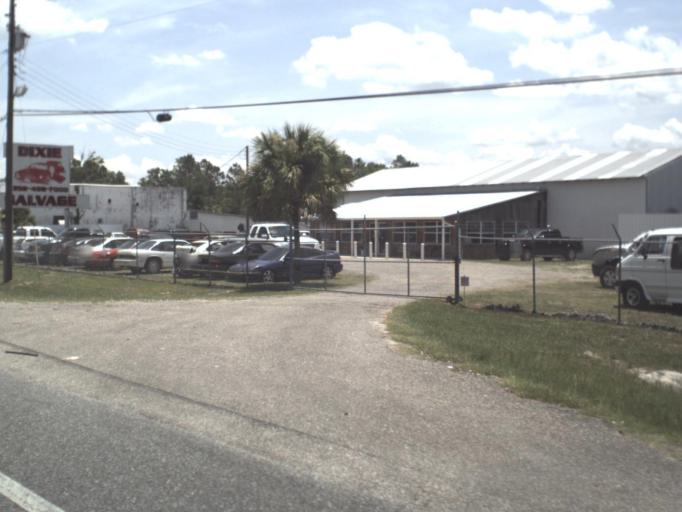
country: US
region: Florida
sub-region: Dixie County
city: Cross City
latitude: 29.6072
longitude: -83.0580
